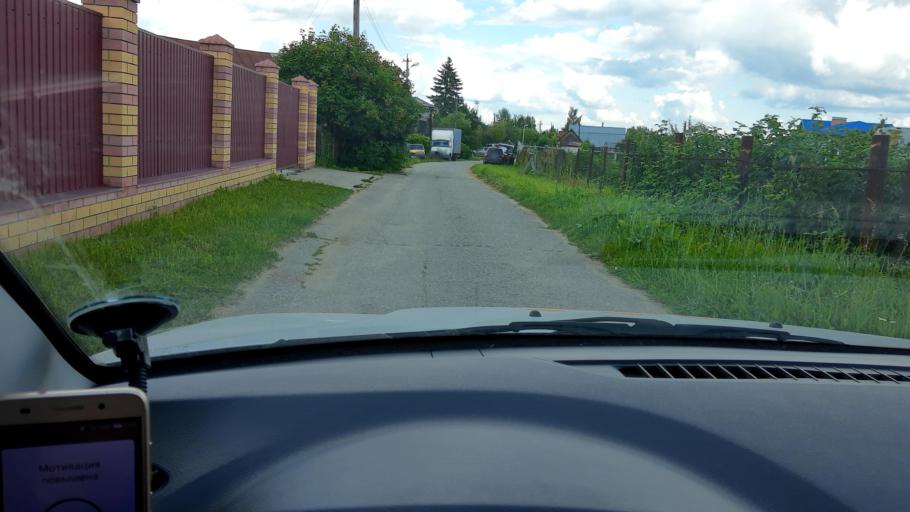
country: RU
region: Nizjnij Novgorod
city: Afonino
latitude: 56.2006
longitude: 44.0313
